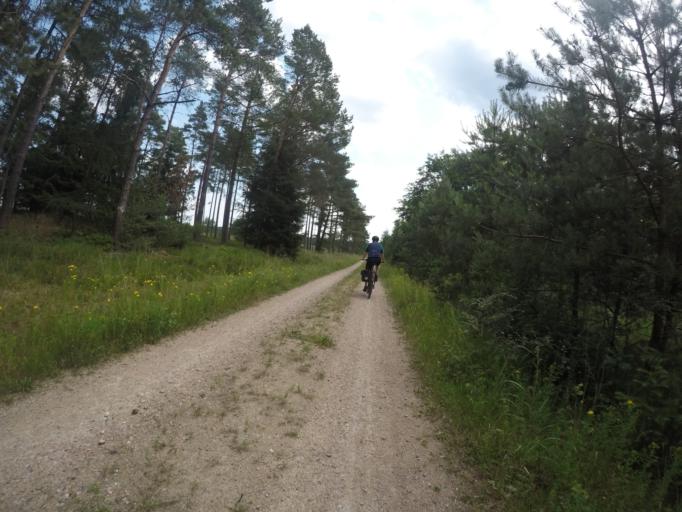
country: DE
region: Lower Saxony
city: Asendorf
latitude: 53.2497
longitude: 9.9541
